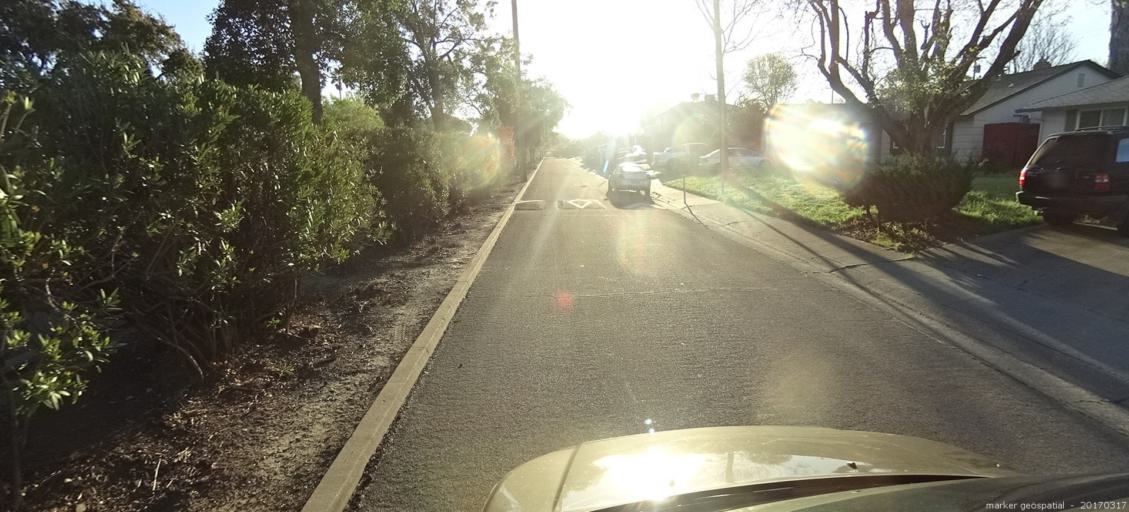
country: US
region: California
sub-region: Sacramento County
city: Parkway
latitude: 38.4955
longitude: -121.4947
